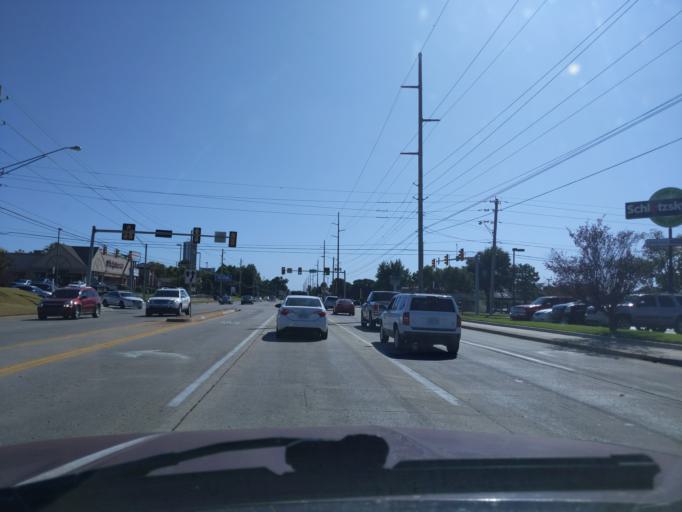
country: US
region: Oklahoma
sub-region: Tulsa County
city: Jenks
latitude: 36.0614
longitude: -95.9579
